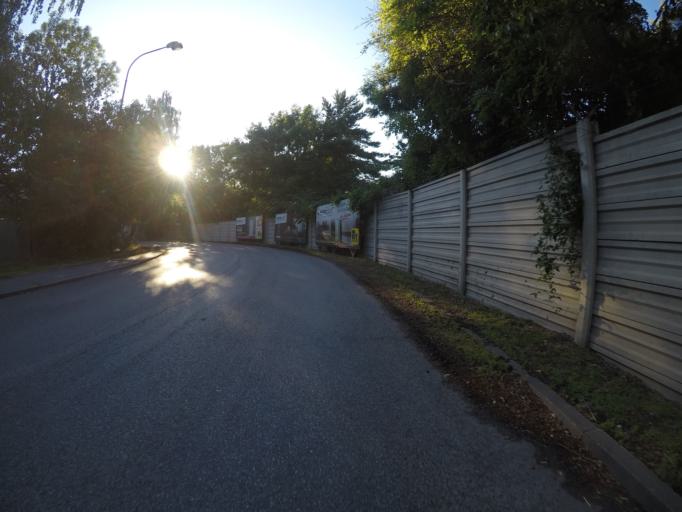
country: SK
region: Bratislavsky
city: Bratislava
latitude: 48.1714
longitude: 17.1558
